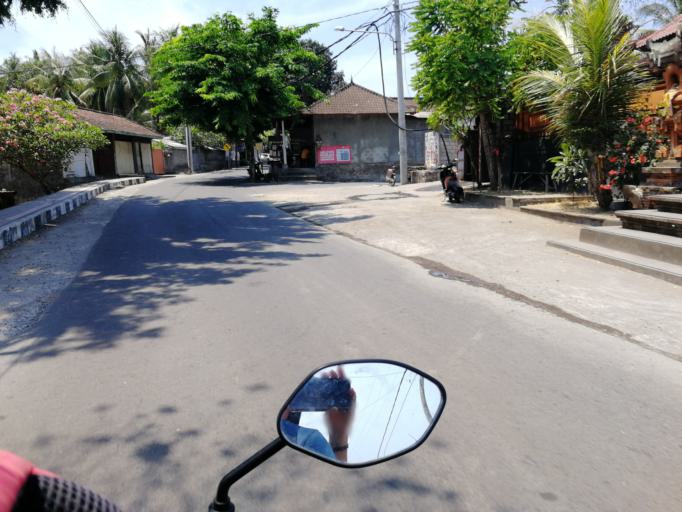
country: ID
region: Bali
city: Banjar Timbrah
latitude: -8.4761
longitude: 115.5963
